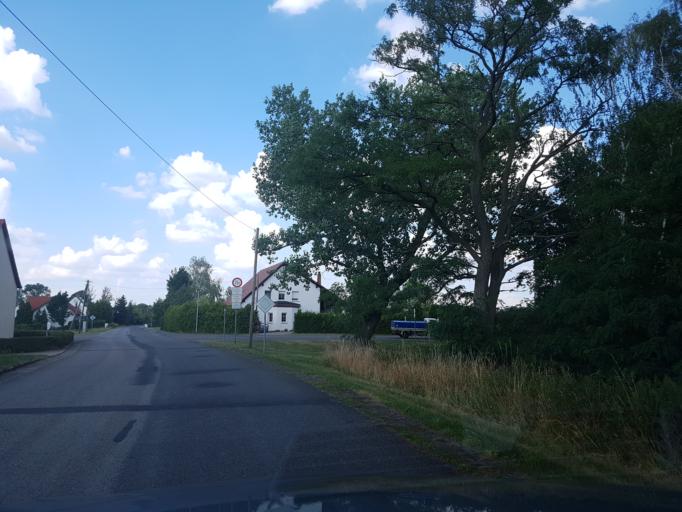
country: DE
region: Brandenburg
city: Schlieben
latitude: 51.6827
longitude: 13.3494
